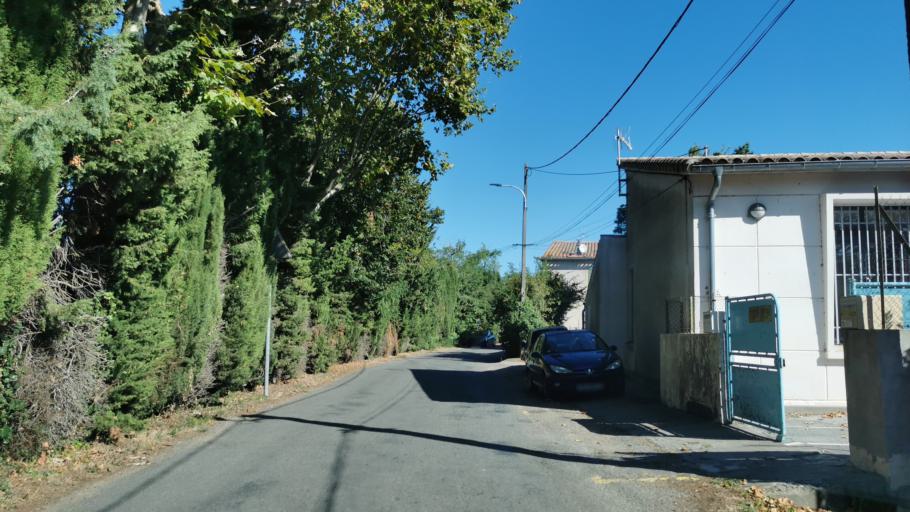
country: FR
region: Languedoc-Roussillon
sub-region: Departement de l'Aude
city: Conques-sur-Orbiel
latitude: 43.2511
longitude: 2.4396
